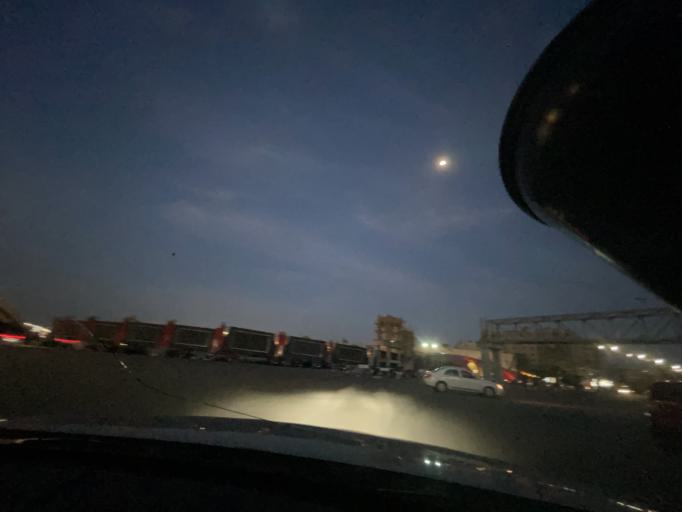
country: EG
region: Muhafazat al Qahirah
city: Cairo
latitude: 30.0710
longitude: 31.3544
